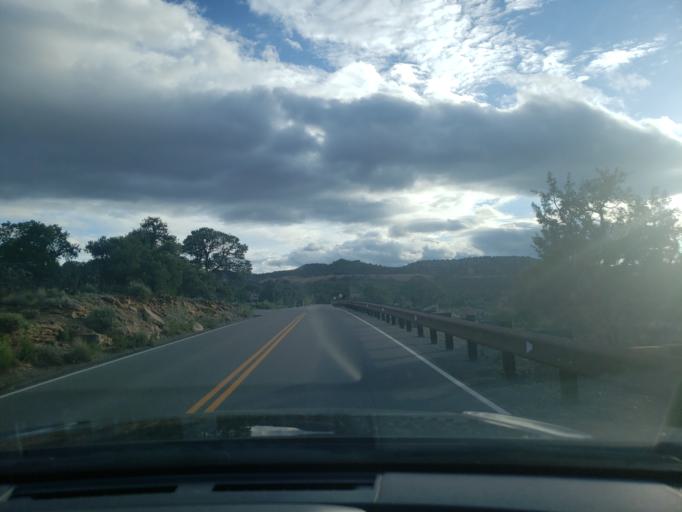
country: US
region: Colorado
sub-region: Mesa County
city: Redlands
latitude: 39.0276
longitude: -108.6573
